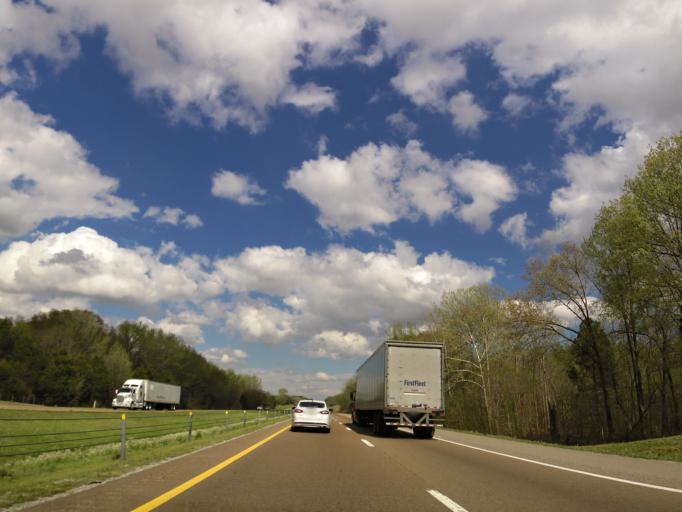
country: US
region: Tennessee
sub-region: Crockett County
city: Bells
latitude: 35.6144
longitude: -89.0084
